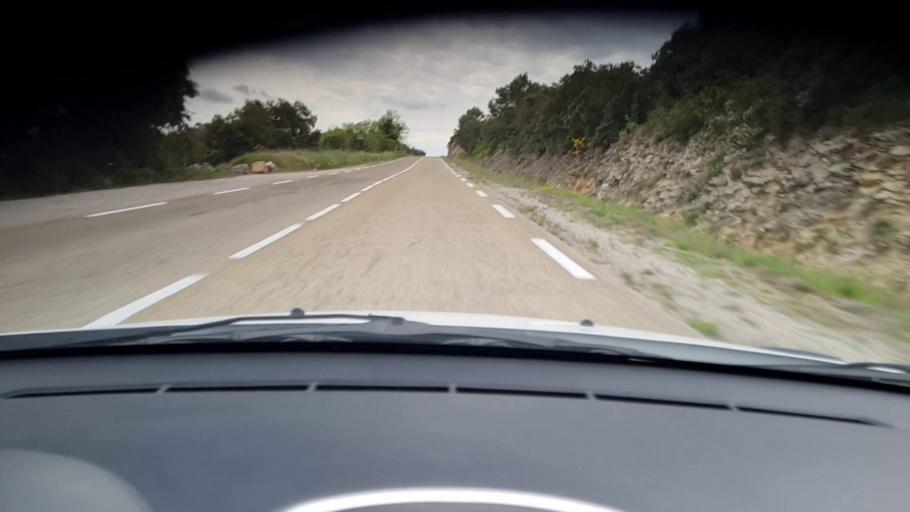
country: FR
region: Languedoc-Roussillon
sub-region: Departement du Gard
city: Poulx
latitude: 43.9107
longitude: 4.3894
